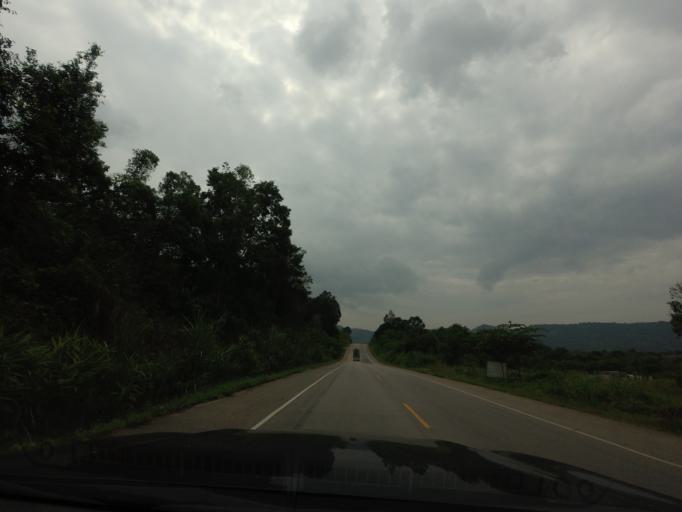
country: TH
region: Loei
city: Dan Sai
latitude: 17.2146
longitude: 101.1715
